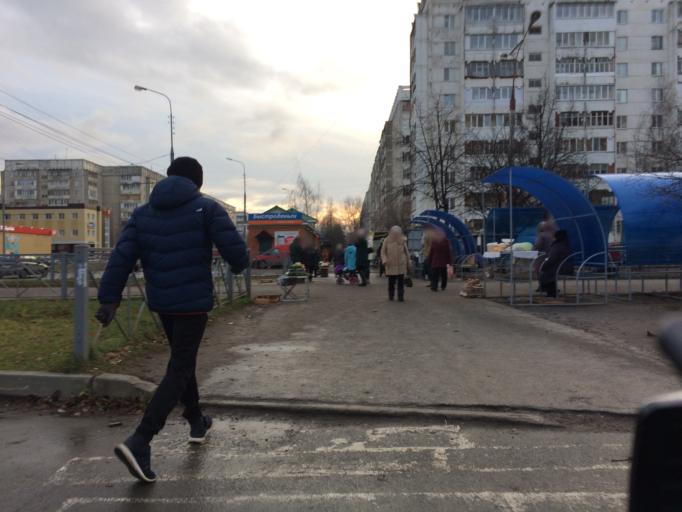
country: RU
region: Mariy-El
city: Yoshkar-Ola
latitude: 56.6309
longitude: 47.9176
